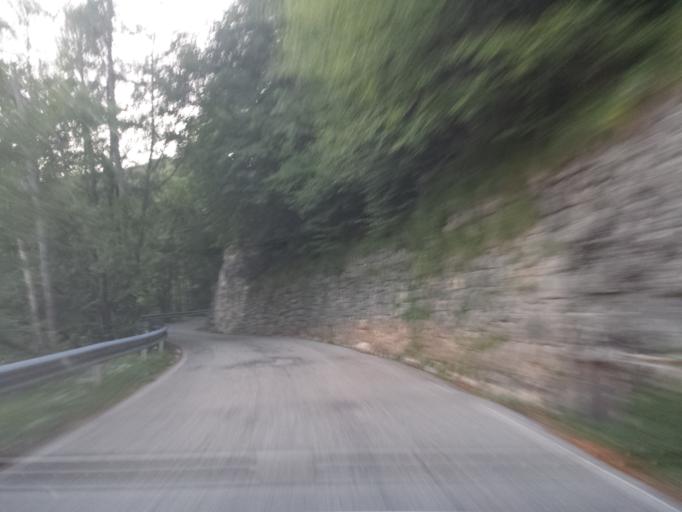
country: IT
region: Veneto
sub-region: Provincia di Vicenza
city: Recoaro Terme
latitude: 45.7219
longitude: 11.1786
